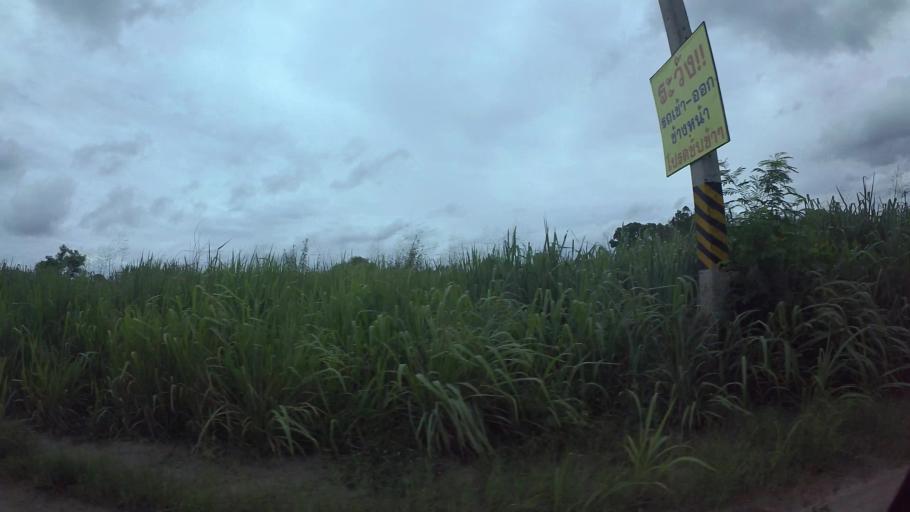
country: TH
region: Chon Buri
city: Si Racha
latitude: 13.1764
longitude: 100.9815
